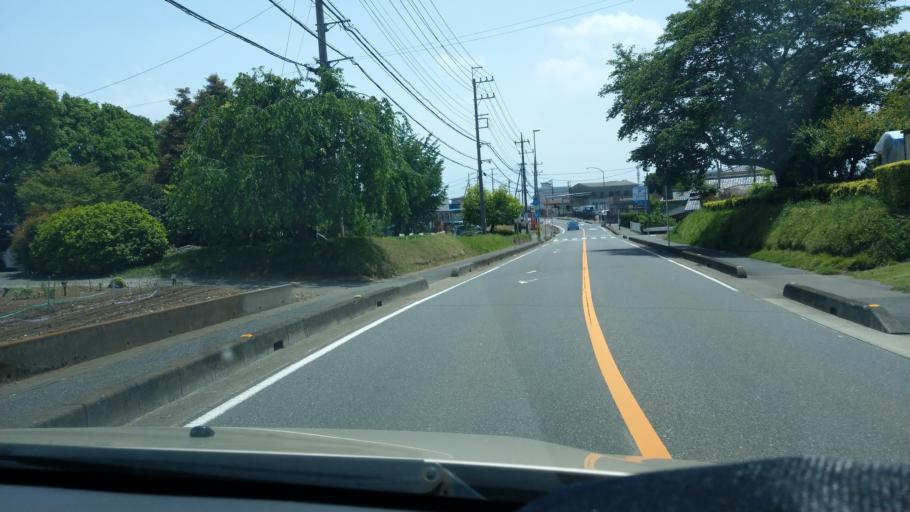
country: JP
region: Saitama
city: Iwatsuki
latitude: 35.9151
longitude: 139.7221
